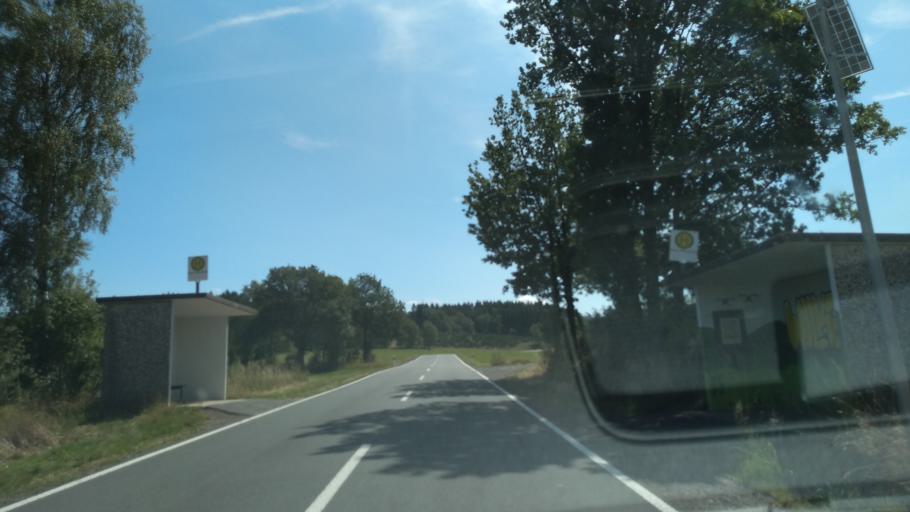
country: DE
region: North Rhine-Westphalia
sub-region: Regierungsbezirk Arnsberg
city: Herscheid
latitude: 51.1048
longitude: 7.7670
